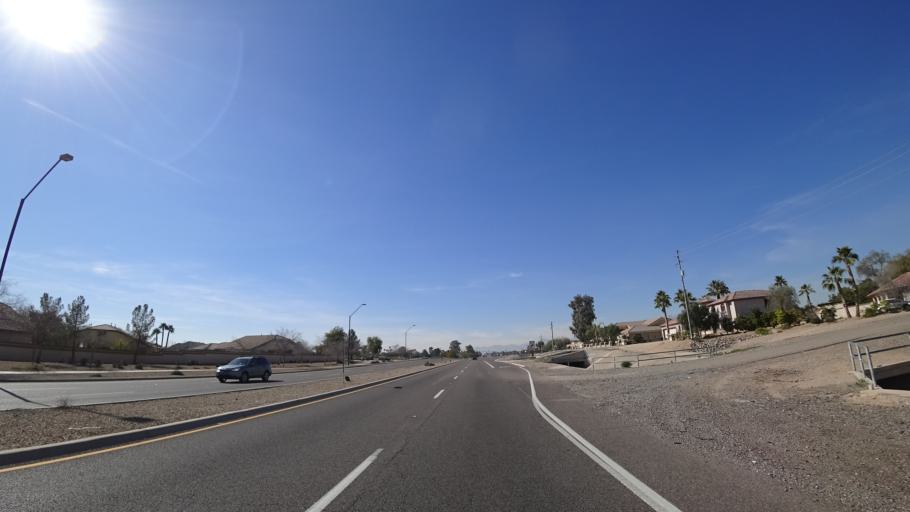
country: US
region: Arizona
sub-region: Maricopa County
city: Litchfield Park
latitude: 33.5076
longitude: -112.3355
